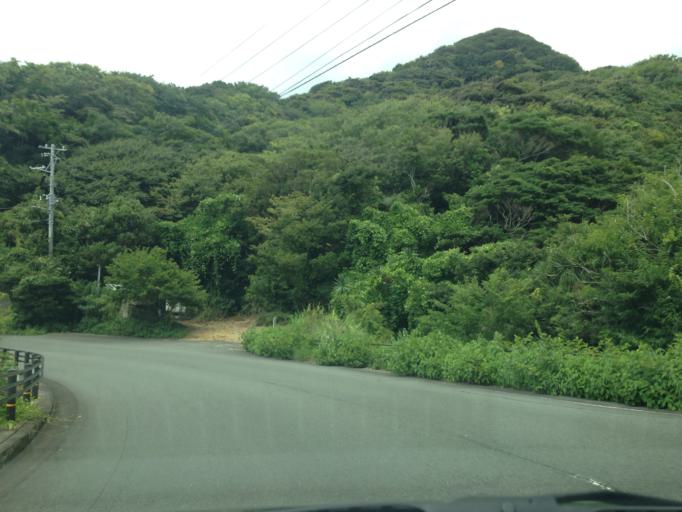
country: JP
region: Shizuoka
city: Shimoda
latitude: 34.6685
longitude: 138.7917
